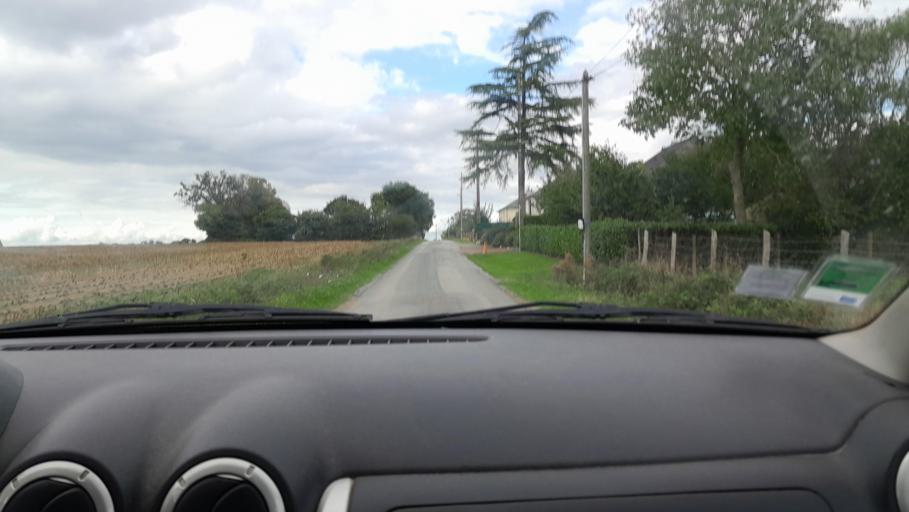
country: FR
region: Brittany
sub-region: Departement d'Ille-et-Vilaine
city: Argentre-du-Plessis
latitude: 48.0553
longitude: -1.1265
